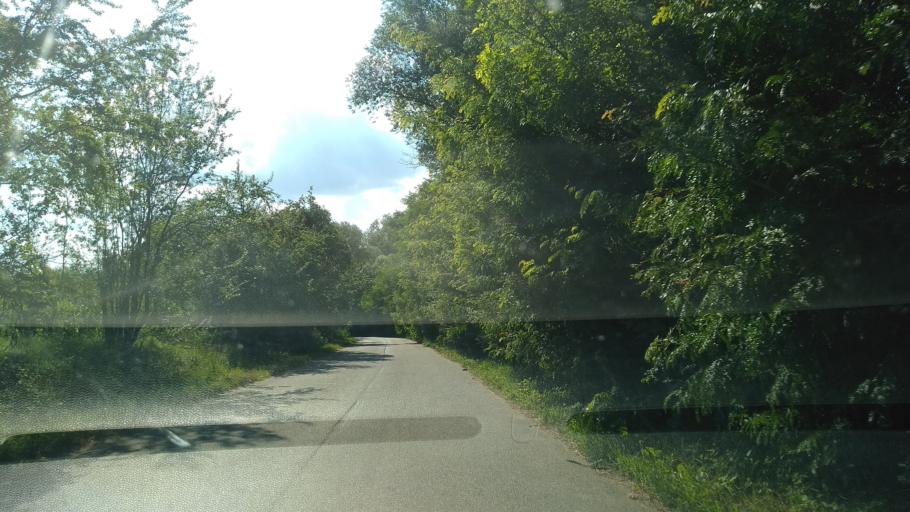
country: RO
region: Hunedoara
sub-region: Comuna Bosorod
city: Bosorod
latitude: 45.7009
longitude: 23.0803
